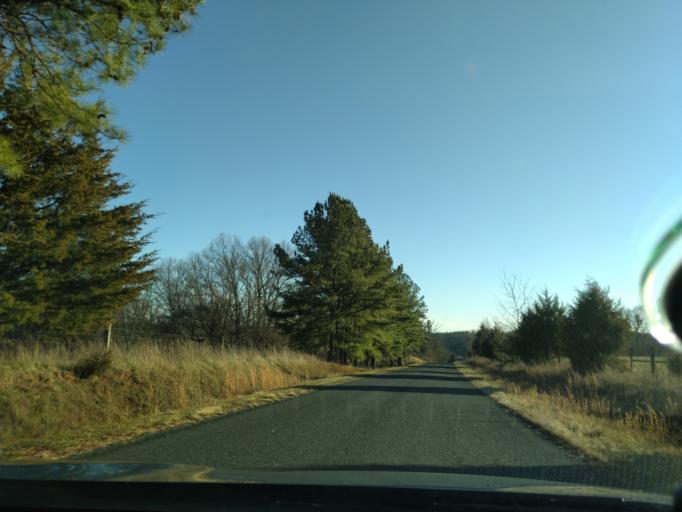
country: US
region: Virginia
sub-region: Appomattox County
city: Appomattox
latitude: 37.3804
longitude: -78.6406
